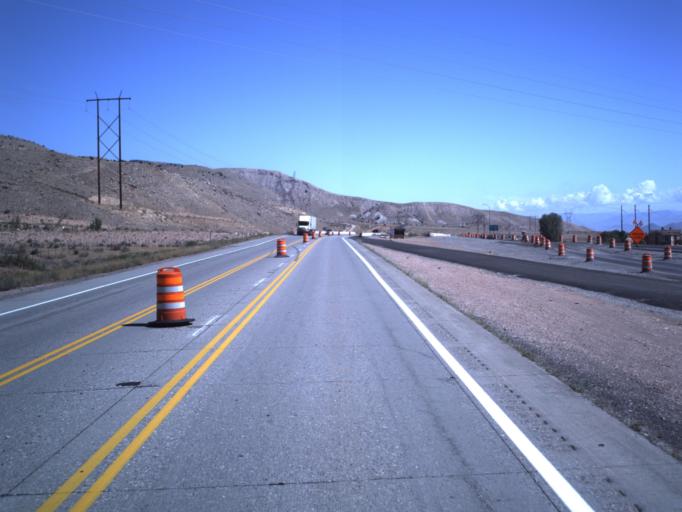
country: US
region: Utah
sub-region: Sevier County
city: Richfield
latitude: 38.7841
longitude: -112.0924
